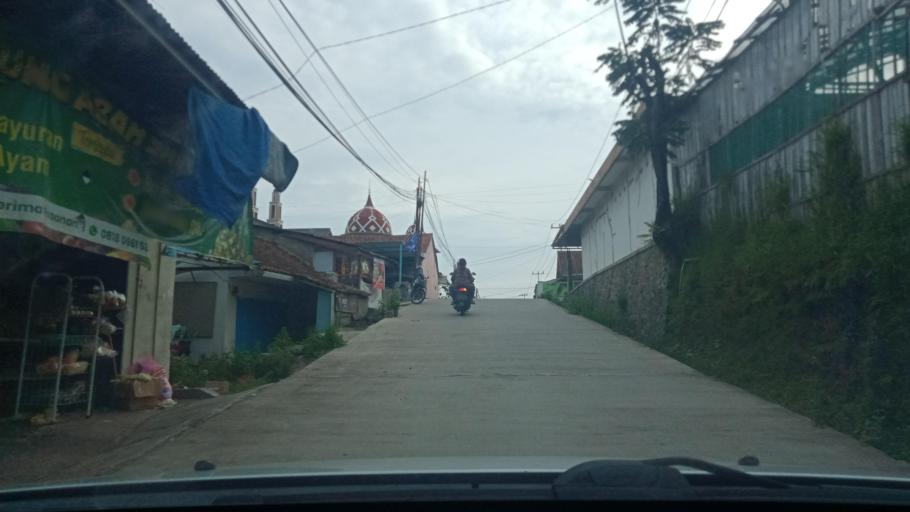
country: ID
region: West Java
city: Lembang
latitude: -6.8076
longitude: 107.5870
